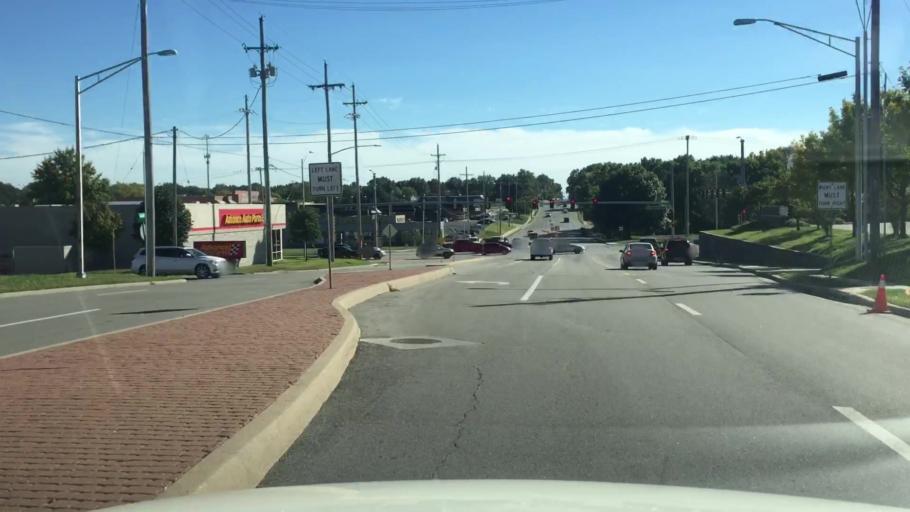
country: US
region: Kansas
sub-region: Johnson County
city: Shawnee
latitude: 39.0158
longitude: -94.7239
